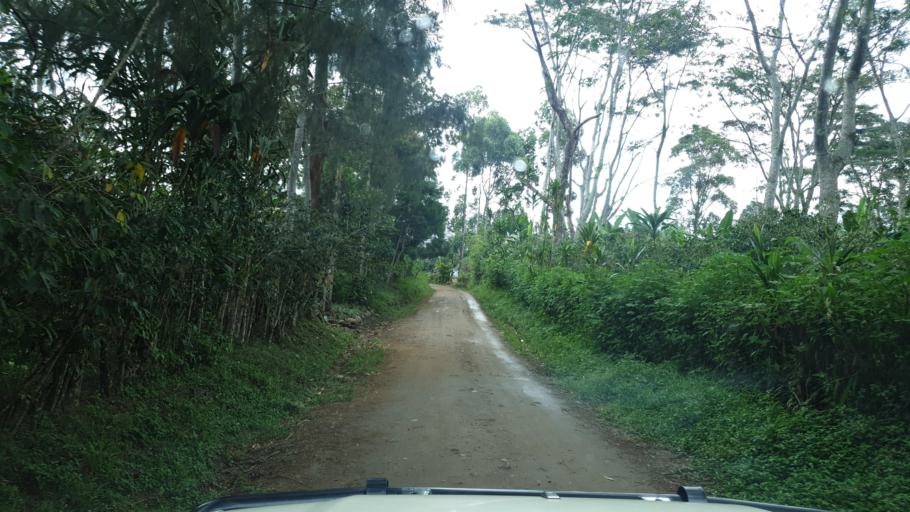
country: PG
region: Eastern Highlands
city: Goroka
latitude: -5.9449
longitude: 145.2713
